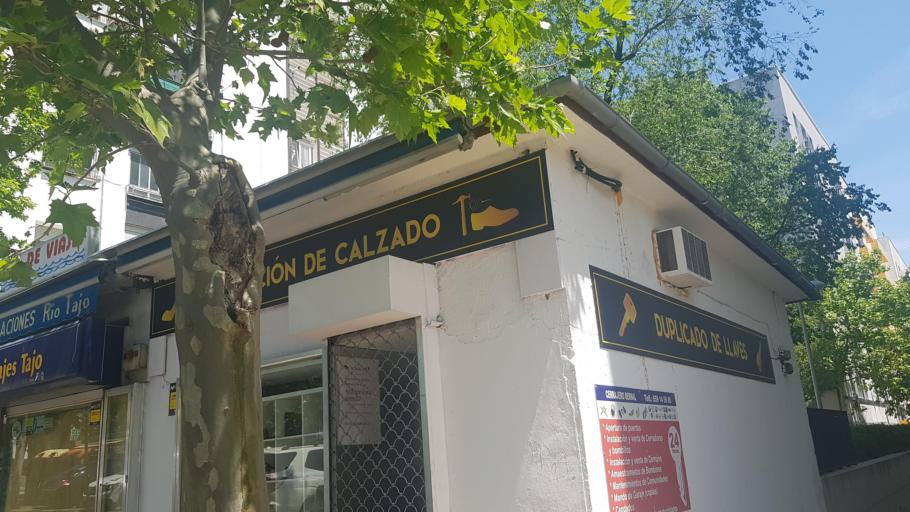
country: ES
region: Madrid
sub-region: Provincia de Madrid
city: Villaverde
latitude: 40.3582
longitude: -3.6960
